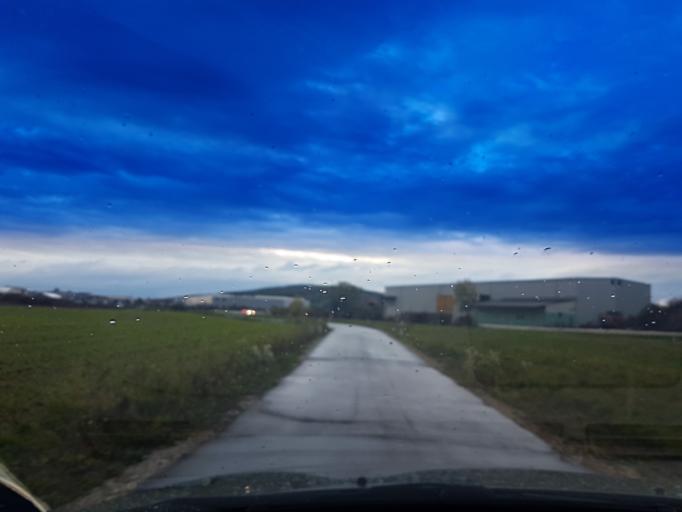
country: DE
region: Bavaria
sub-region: Upper Franconia
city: Pettstadt
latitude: 49.8294
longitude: 10.9473
